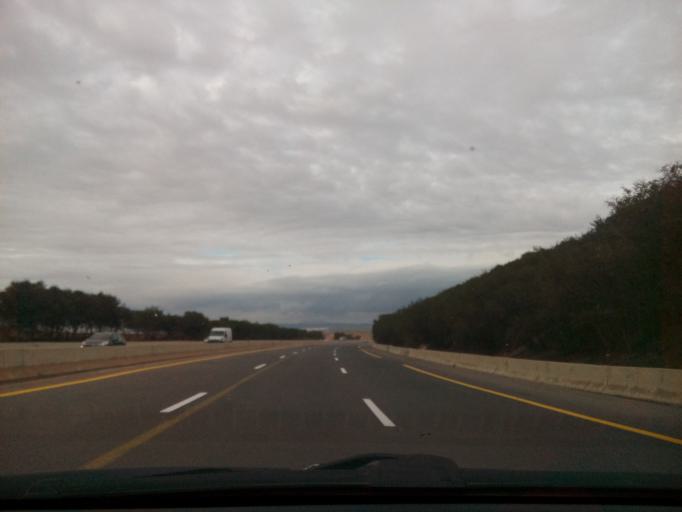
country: DZ
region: Sidi Bel Abbes
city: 'Ain el Berd
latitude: 35.4728
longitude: -0.3842
